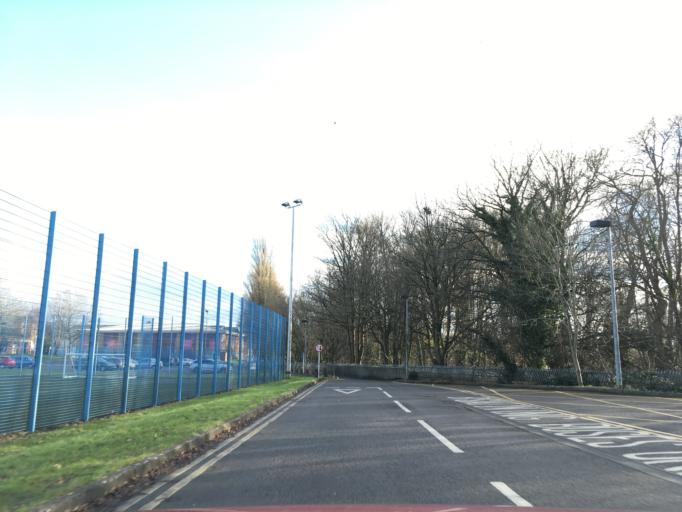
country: GB
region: Wales
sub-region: Cardiff
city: Cardiff
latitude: 51.4986
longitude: -3.2004
